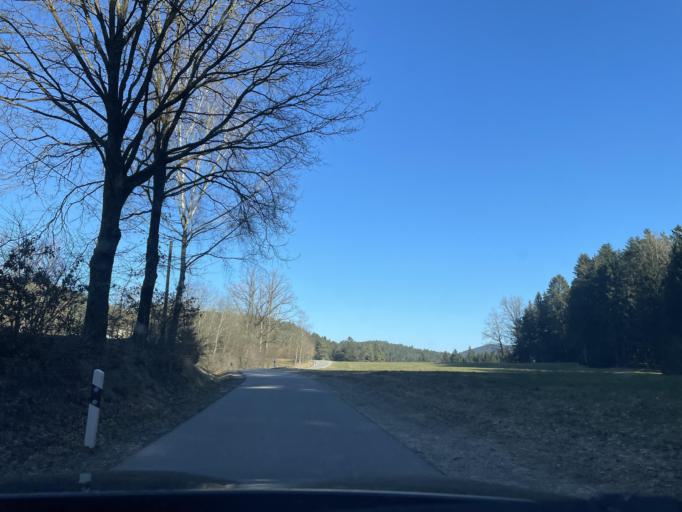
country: DE
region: Bavaria
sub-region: Lower Bavaria
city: Viechtach
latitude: 49.0719
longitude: 12.9263
